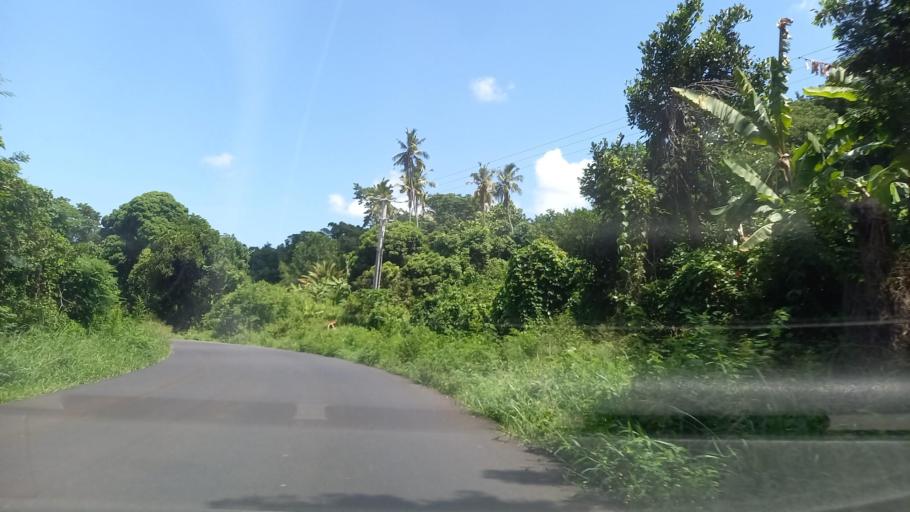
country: YT
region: M'Tsangamouji
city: M'Tsangamouji
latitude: -12.7553
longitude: 45.0659
